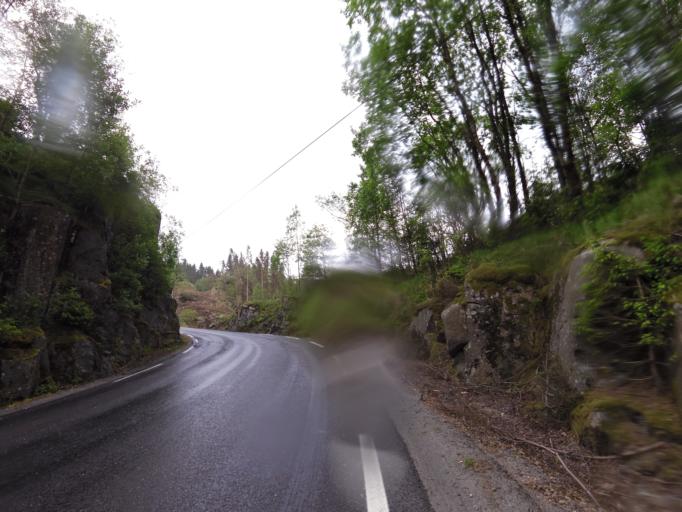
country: NO
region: Vest-Agder
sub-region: Lyngdal
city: Lyngdal
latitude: 58.1122
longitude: 7.0835
